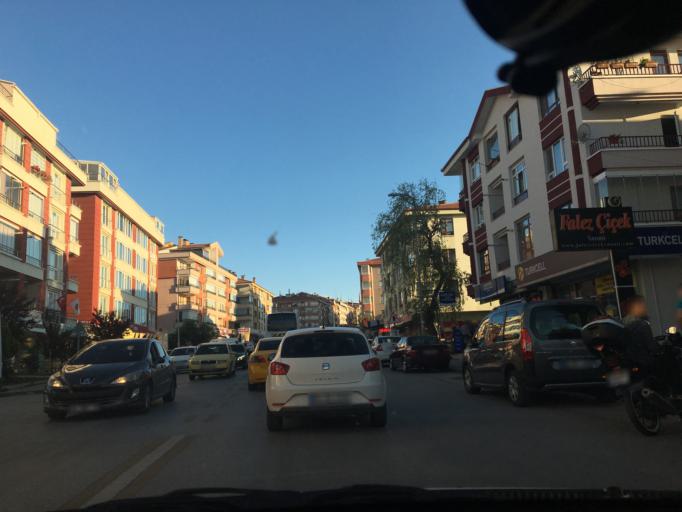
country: TR
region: Ankara
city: Ankara
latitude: 39.8865
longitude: 32.8288
